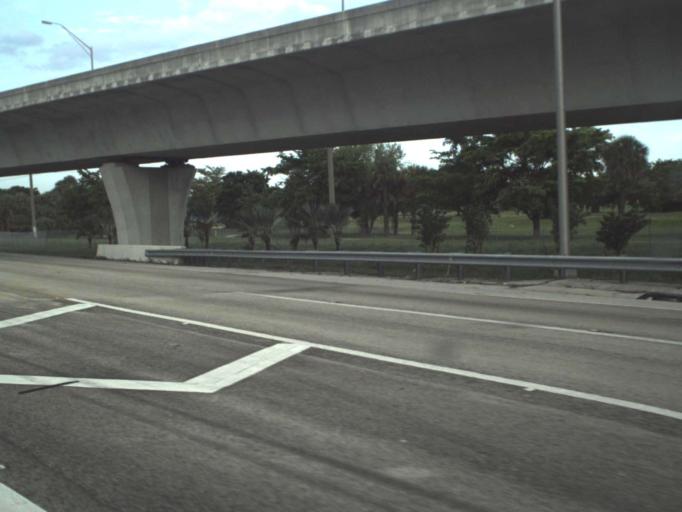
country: US
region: Florida
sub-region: Palm Beach County
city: Lake Clarke Shores
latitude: 26.6797
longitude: -80.0694
